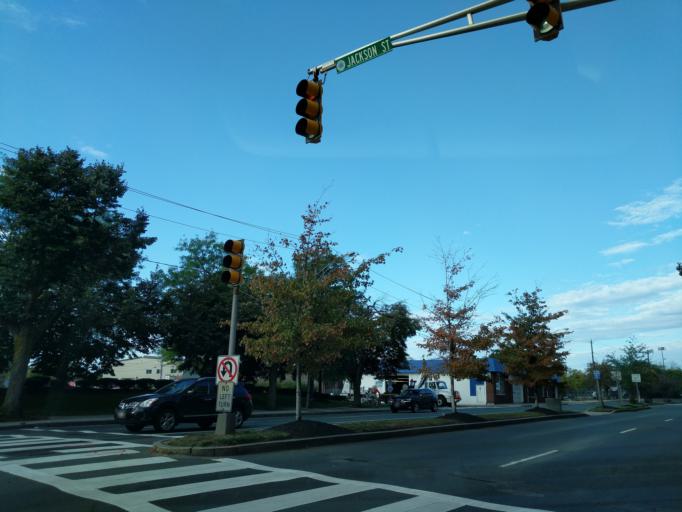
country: US
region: Massachusetts
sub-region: Middlesex County
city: Malden
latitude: 42.4255
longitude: -71.0716
